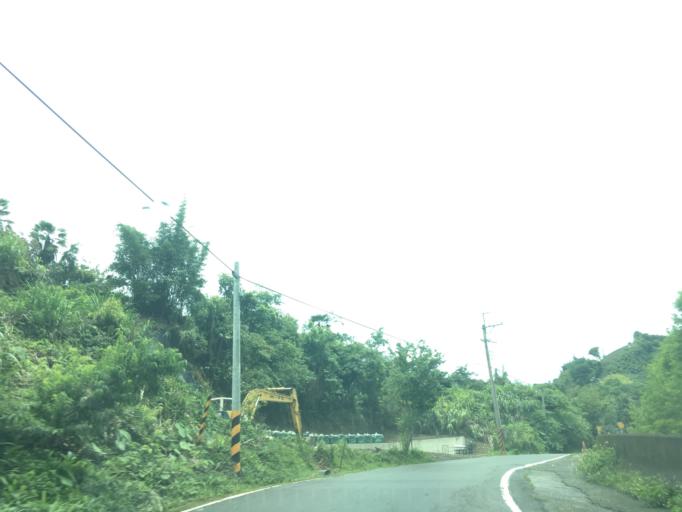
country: TW
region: Taiwan
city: Lugu
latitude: 23.5478
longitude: 120.6867
